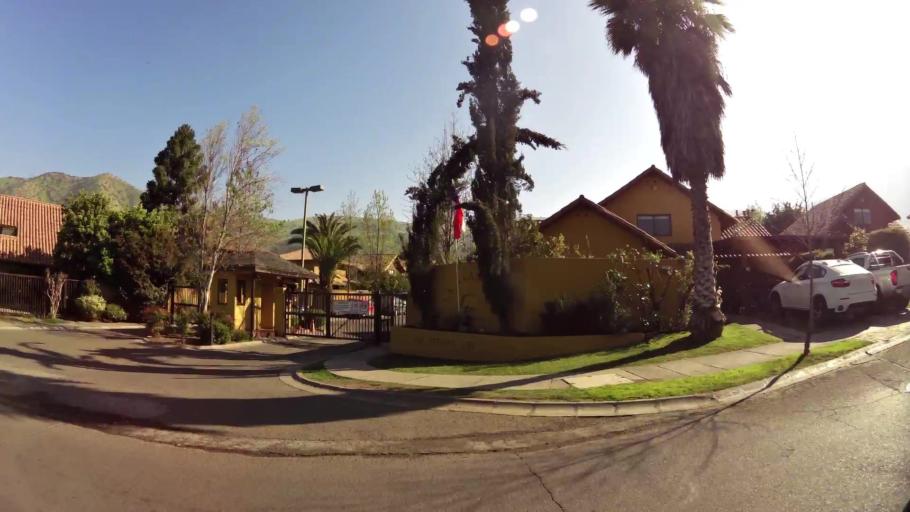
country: CL
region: Santiago Metropolitan
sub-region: Provincia de Chacabuco
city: Chicureo Abajo
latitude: -33.3450
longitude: -70.6675
